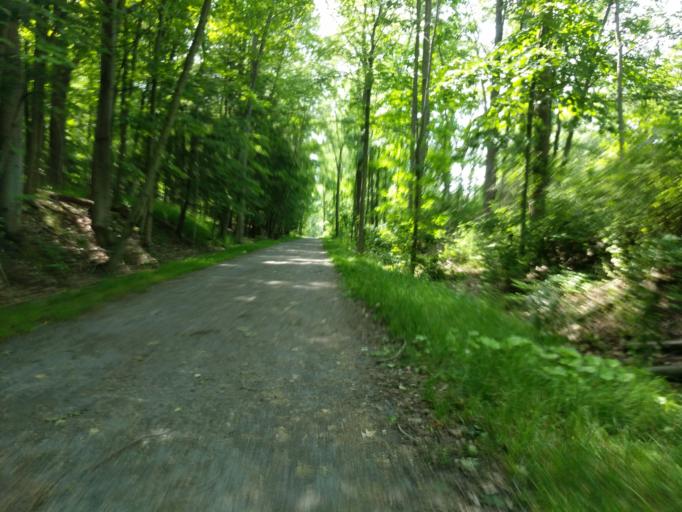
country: US
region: New York
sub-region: Tompkins County
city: Trumansburg
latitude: 42.5306
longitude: -76.6098
